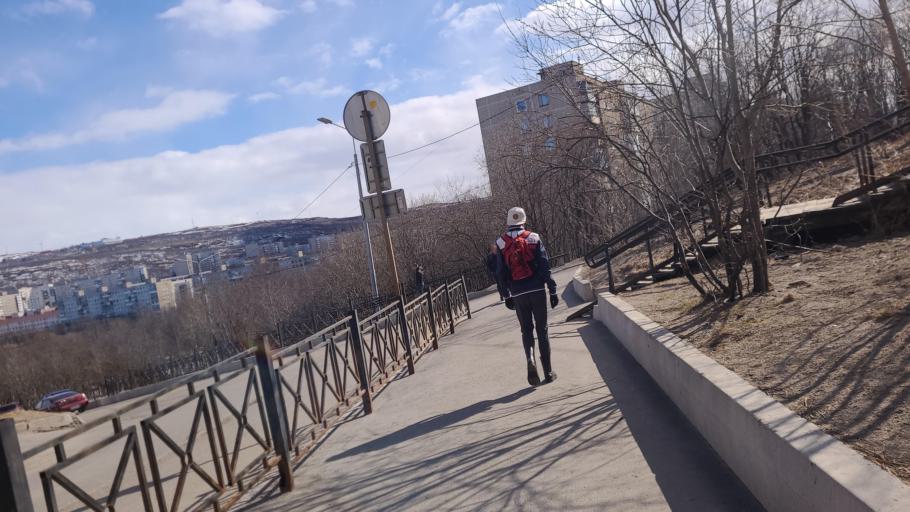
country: RU
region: Murmansk
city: Murmansk
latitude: 68.9423
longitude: 33.1000
